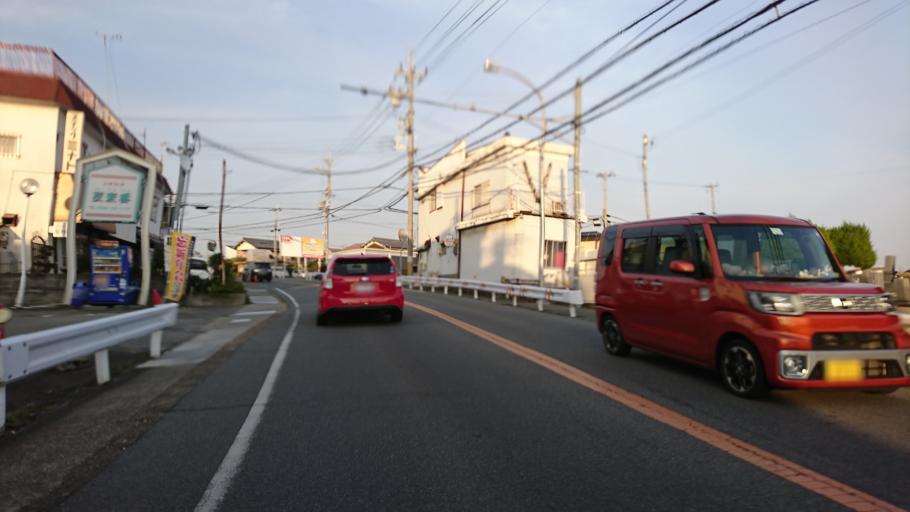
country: JP
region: Hyogo
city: Kakogawacho-honmachi
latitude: 34.7586
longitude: 134.8745
